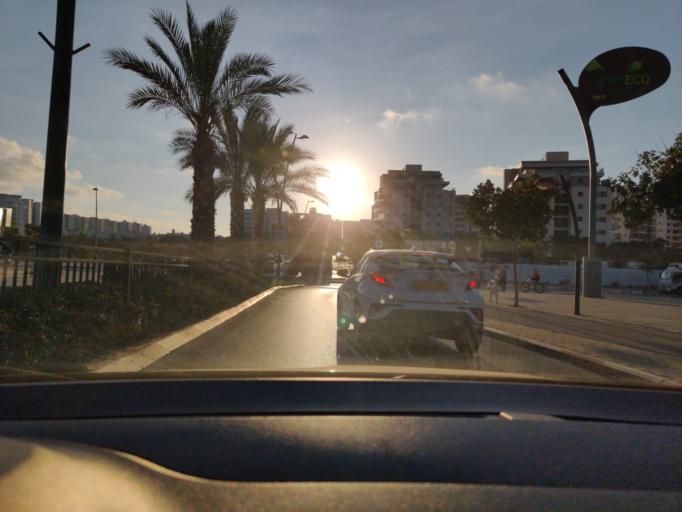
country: IL
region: Central District
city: Elyakhin
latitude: 32.4278
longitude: 34.9334
